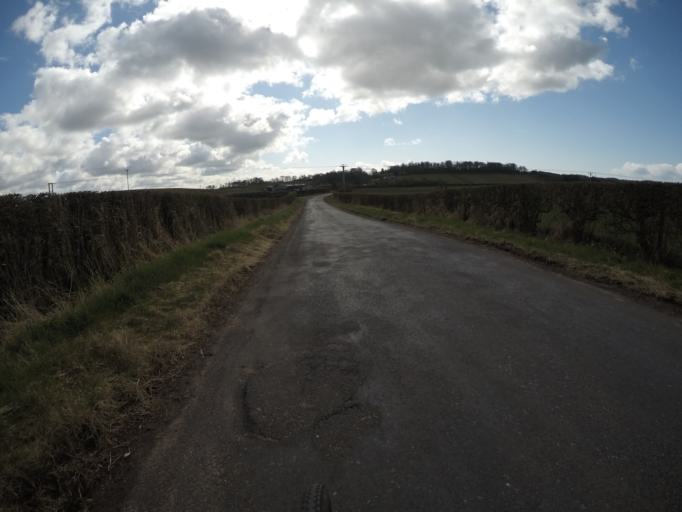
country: GB
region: Scotland
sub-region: South Ayrshire
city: Dundonald
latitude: 55.5893
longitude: -4.5781
